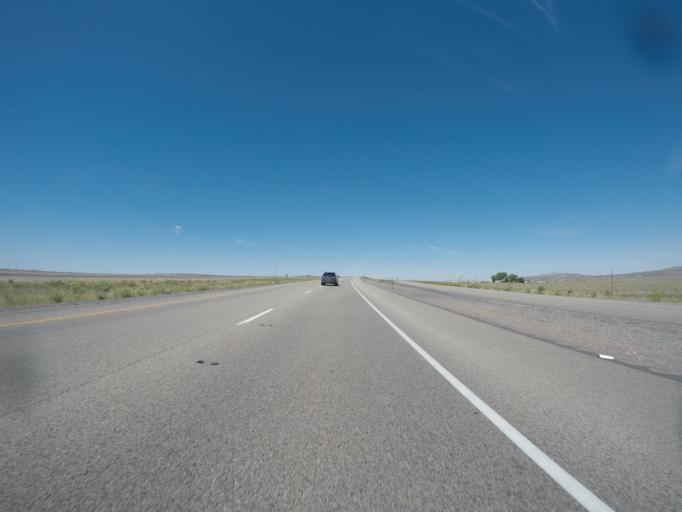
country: US
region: Wyoming
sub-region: Carbon County
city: Saratoga
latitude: 41.7414
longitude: -106.8249
